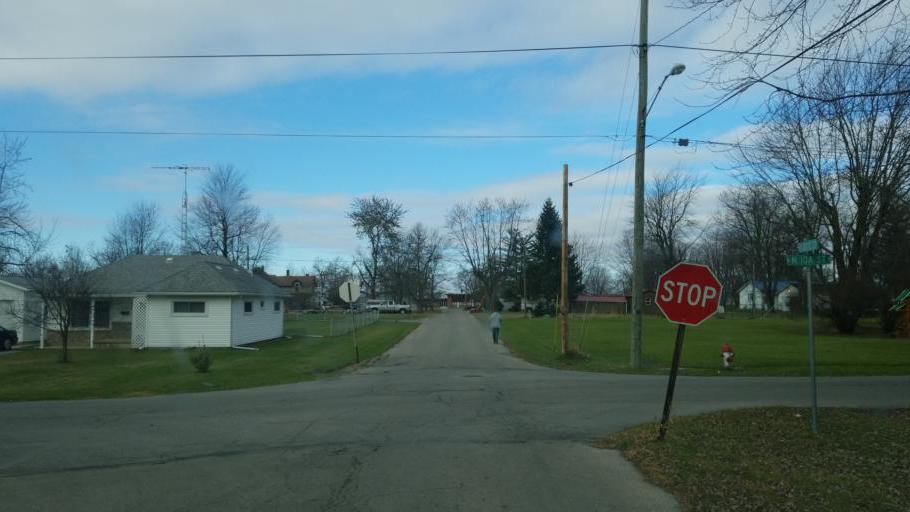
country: US
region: Ohio
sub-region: Hardin County
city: Kenton
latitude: 40.6527
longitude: -83.6180
